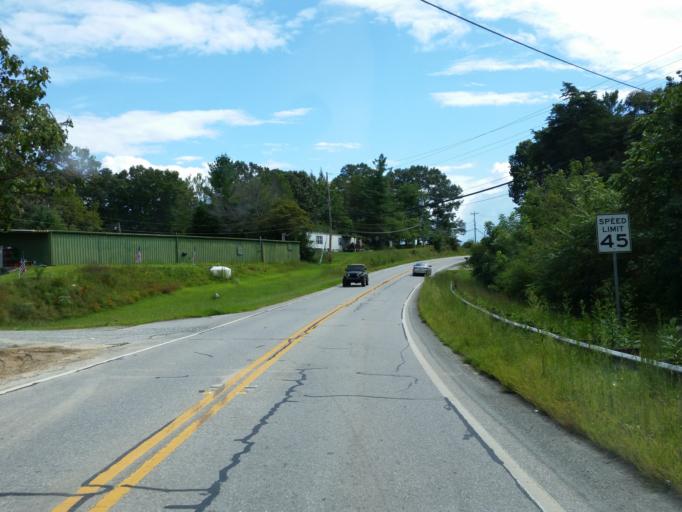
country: US
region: Georgia
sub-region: Fannin County
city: Blue Ridge
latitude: 34.8916
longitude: -84.2611
